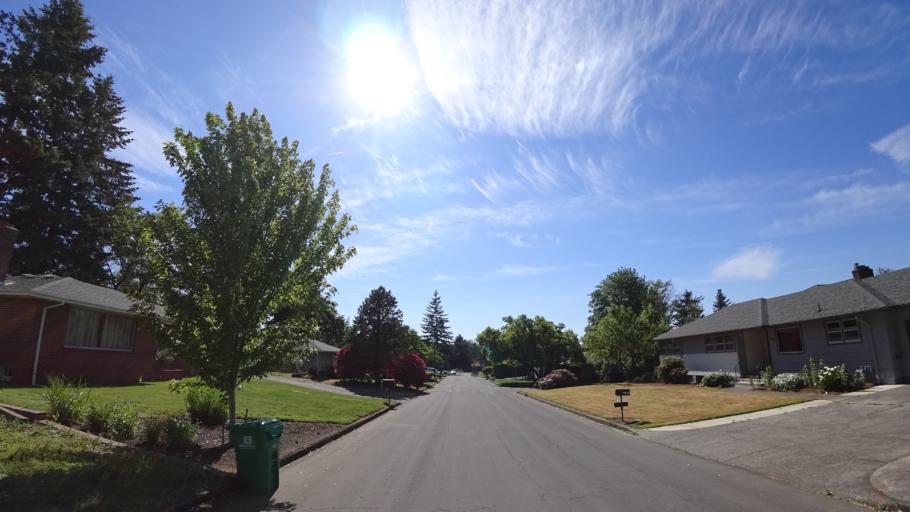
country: US
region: Oregon
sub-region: Multnomah County
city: Gresham
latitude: 45.5003
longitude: -122.4735
